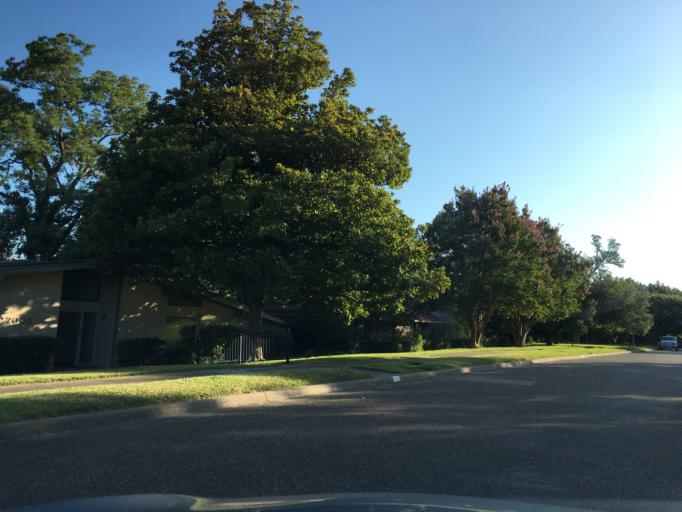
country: US
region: Texas
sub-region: Dallas County
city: Highland Park
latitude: 32.8601
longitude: -96.7401
